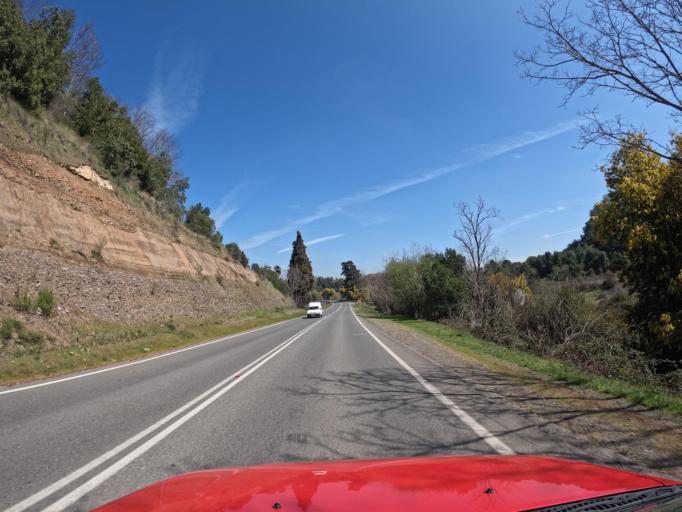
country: CL
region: Maule
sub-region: Provincia de Talca
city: San Clemente
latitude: -35.4671
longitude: -71.2728
